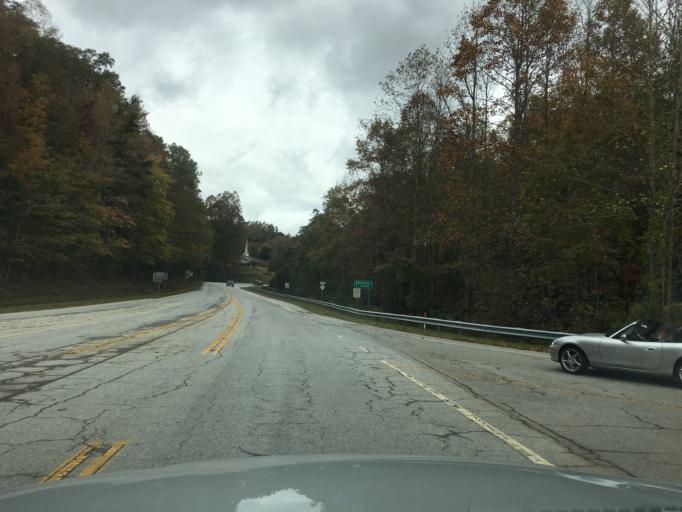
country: US
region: North Carolina
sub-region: Henderson County
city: Flat Rock
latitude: 35.2386
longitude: -82.4158
